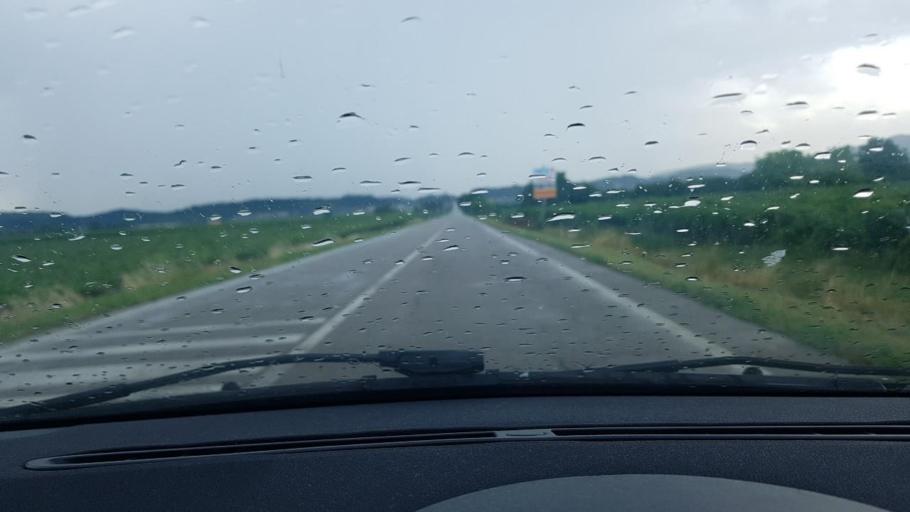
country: IT
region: Veneto
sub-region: Provincia di Verona
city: Caprino Veronese
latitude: 45.5968
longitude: 10.7733
